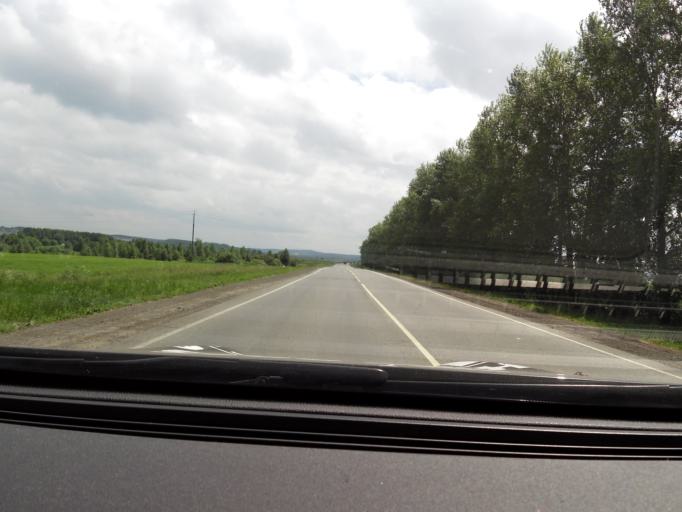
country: RU
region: Perm
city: Kukushtan
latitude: 57.5191
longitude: 56.6335
